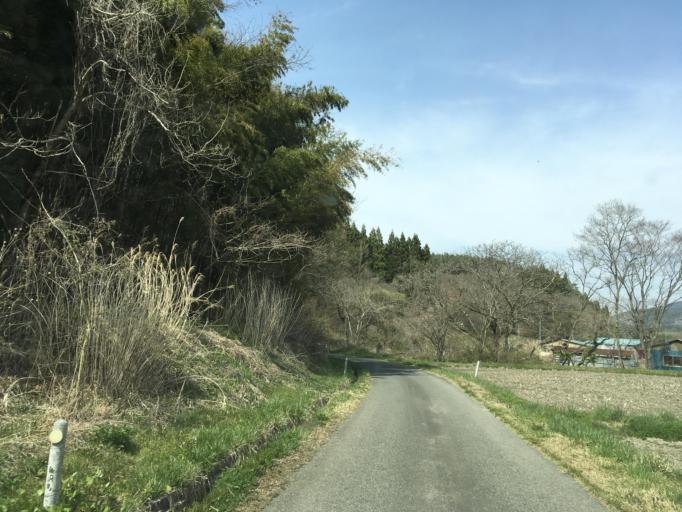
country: JP
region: Iwate
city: Ichinoseki
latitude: 38.8230
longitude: 141.3471
